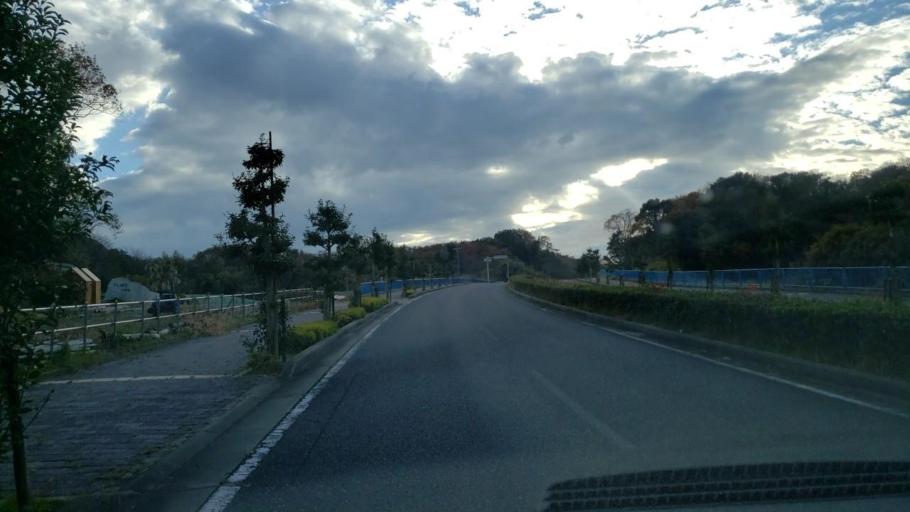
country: JP
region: Hyogo
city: Akashi
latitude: 34.5791
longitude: 135.0039
